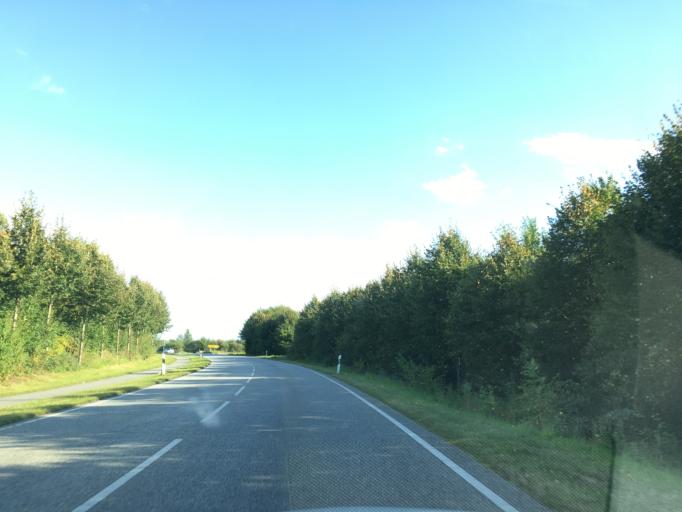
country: DE
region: Schleswig-Holstein
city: Heikendorf
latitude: 54.3607
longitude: 10.2035
